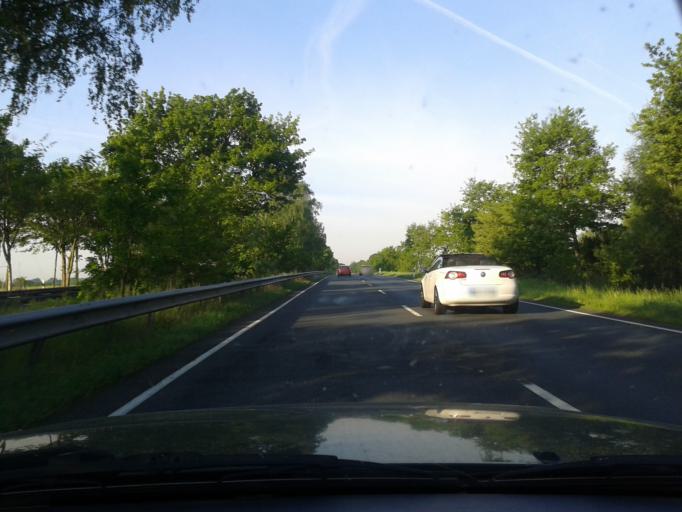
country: DE
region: Lower Saxony
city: Burgdorf
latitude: 52.4811
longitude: 9.9856
